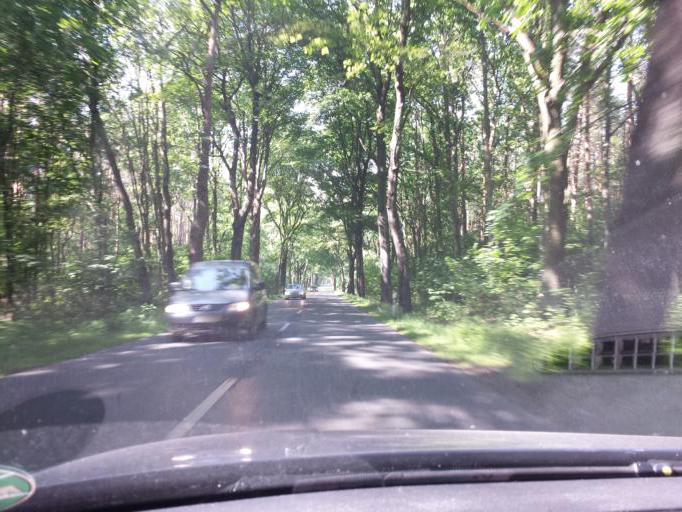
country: DE
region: Brandenburg
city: Kremmen
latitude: 52.8230
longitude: 13.0168
